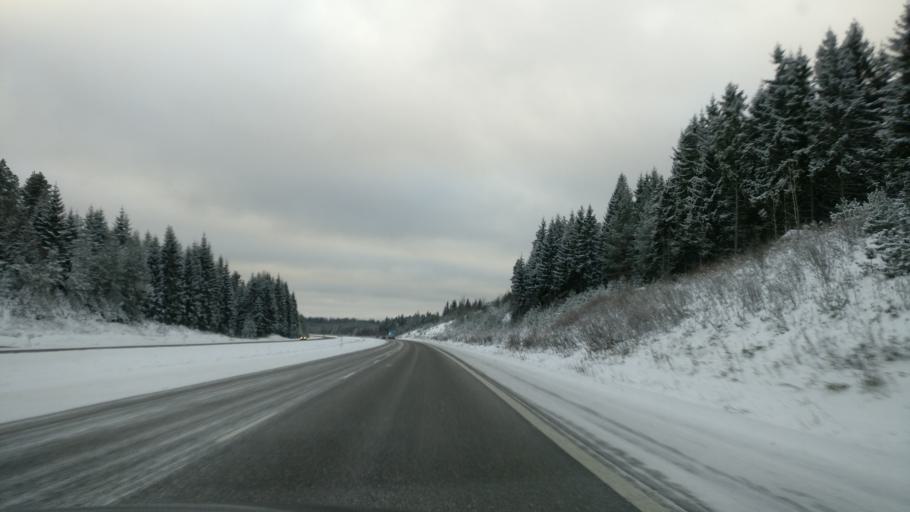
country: FI
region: Paijanne Tavastia
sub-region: Lahti
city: Nastola
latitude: 61.0613
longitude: 25.8643
